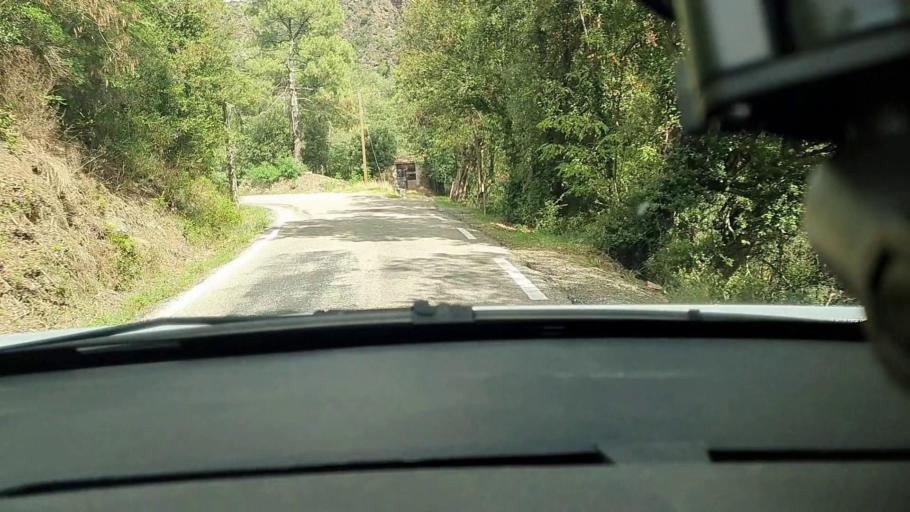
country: FR
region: Languedoc-Roussillon
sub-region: Departement du Gard
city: Besseges
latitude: 44.2991
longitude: 4.0267
